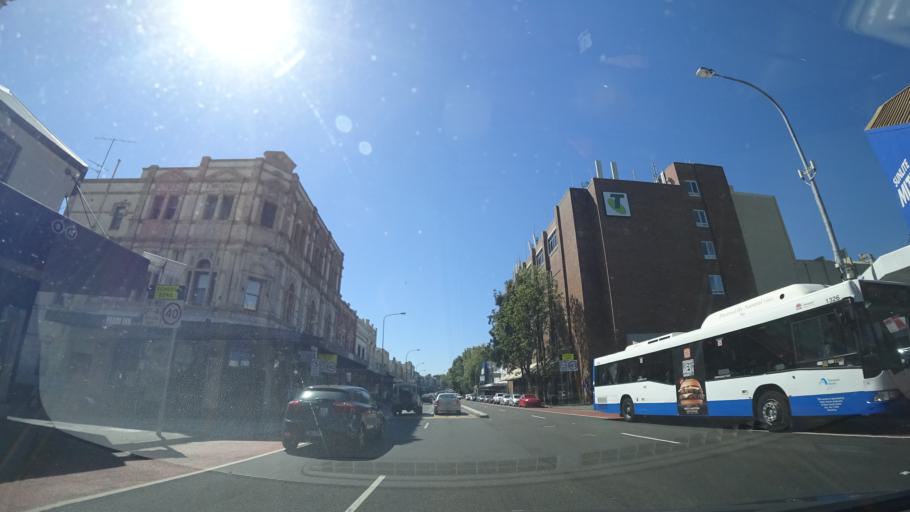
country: AU
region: New South Wales
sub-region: Woollahra
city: Paddington
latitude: -33.8860
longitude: 151.2288
